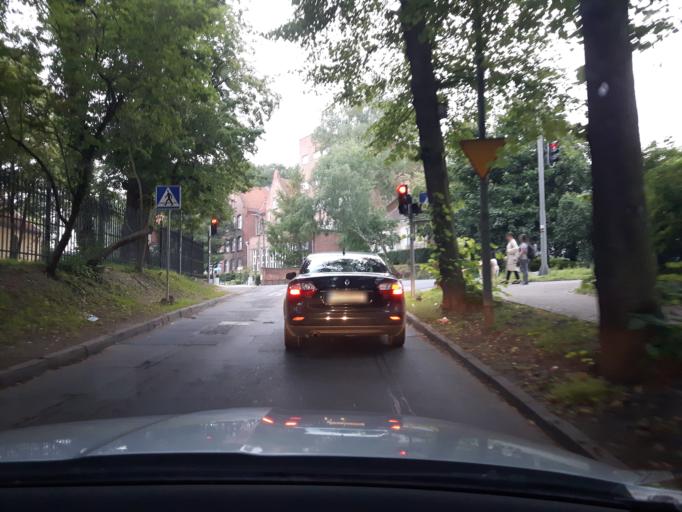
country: PL
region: Pomeranian Voivodeship
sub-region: Sopot
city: Sopot
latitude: 54.4122
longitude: 18.5572
